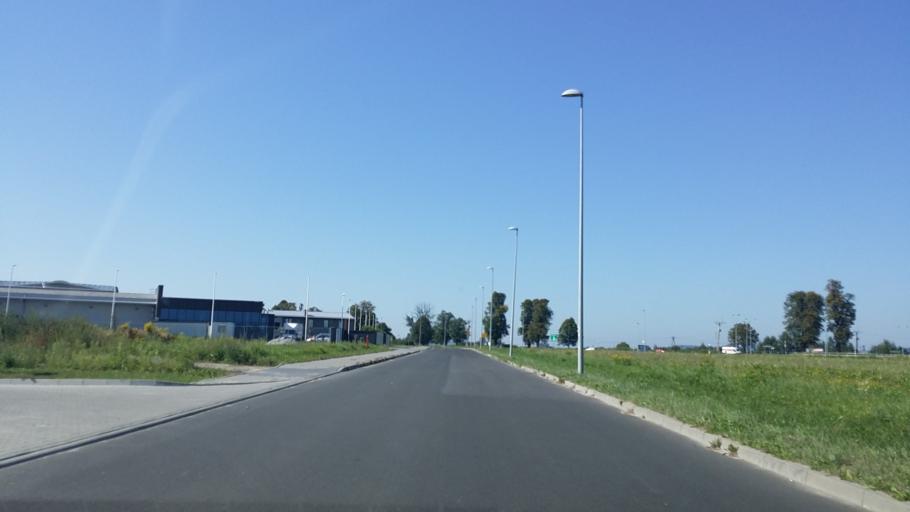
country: PL
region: Lesser Poland Voivodeship
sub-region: Powiat oswiecimski
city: Zator
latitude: 49.9959
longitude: 19.4213
